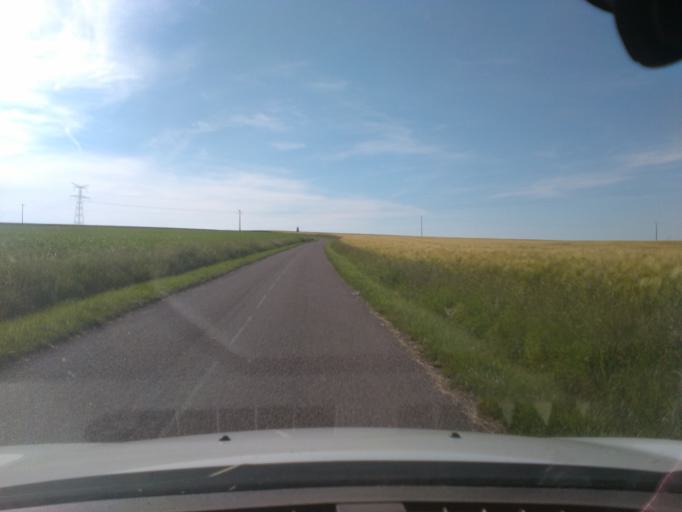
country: FR
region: Lorraine
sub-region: Departement des Vosges
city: Mirecourt
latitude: 48.2890
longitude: 6.1664
